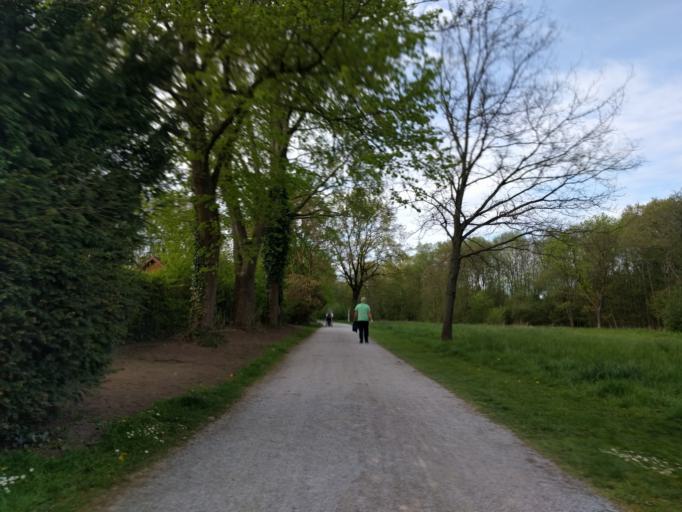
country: DE
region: North Rhine-Westphalia
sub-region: Regierungsbezirk Detmold
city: Bielefeld
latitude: 52.0535
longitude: 8.5319
